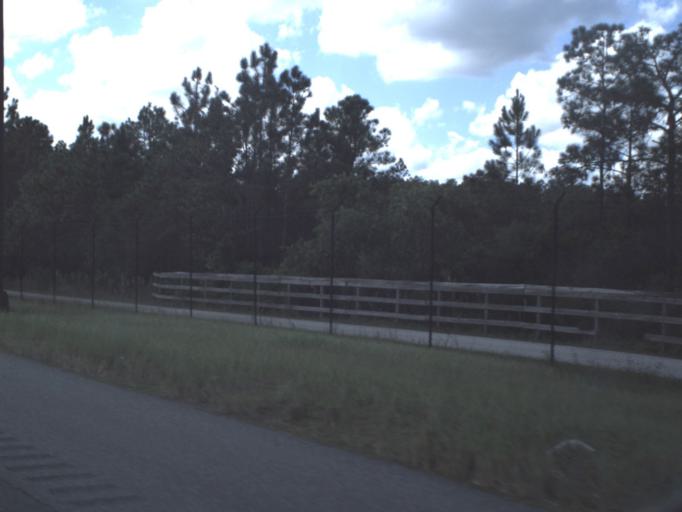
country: US
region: Florida
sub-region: Pasco County
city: Odessa
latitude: 28.2571
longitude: -82.5507
